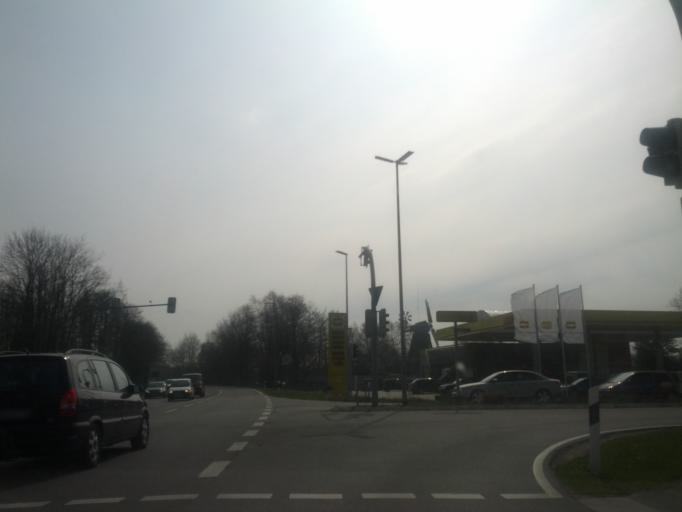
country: DE
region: Lower Saxony
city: Osteel
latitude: 53.5290
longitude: 7.2700
